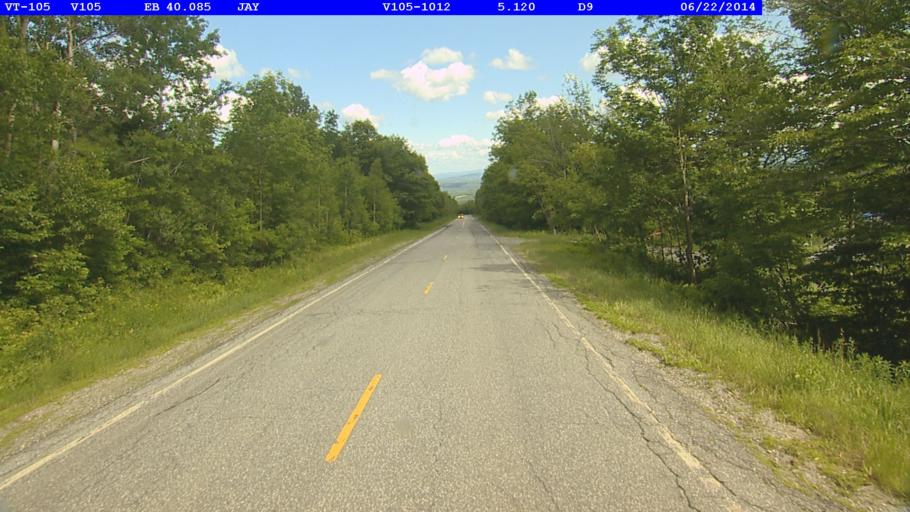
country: CA
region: Quebec
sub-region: Monteregie
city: Sutton
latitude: 44.9796
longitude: -72.4829
